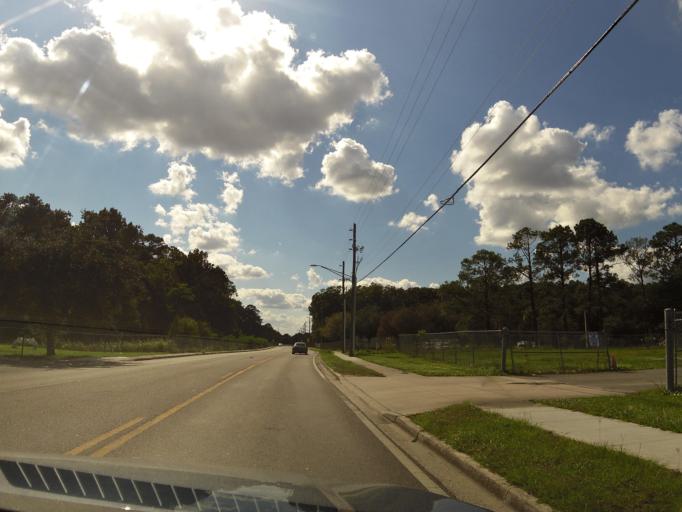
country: US
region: Florida
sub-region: Duval County
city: Jacksonville
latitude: 30.3439
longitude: -81.7264
